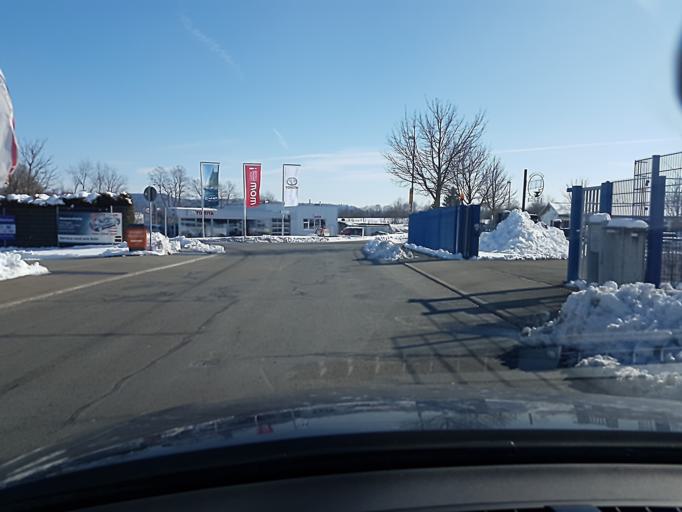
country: DE
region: Baden-Wuerttemberg
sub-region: Freiburg Region
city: Rottweil
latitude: 48.1785
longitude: 8.6316
